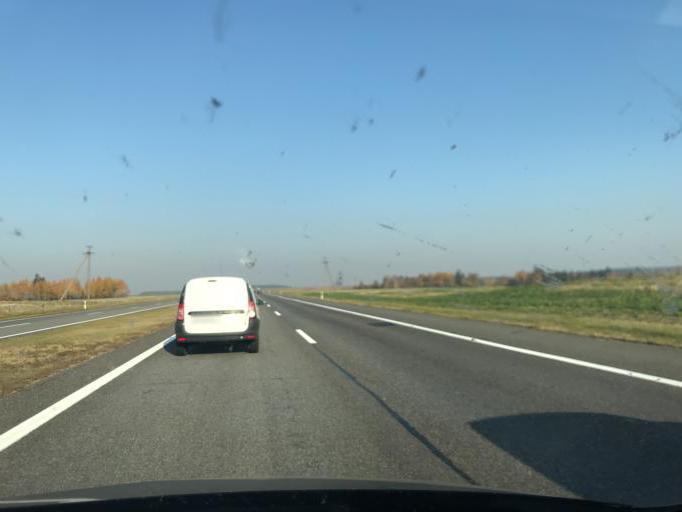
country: BY
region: Minsk
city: Snow
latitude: 53.2799
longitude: 26.3178
